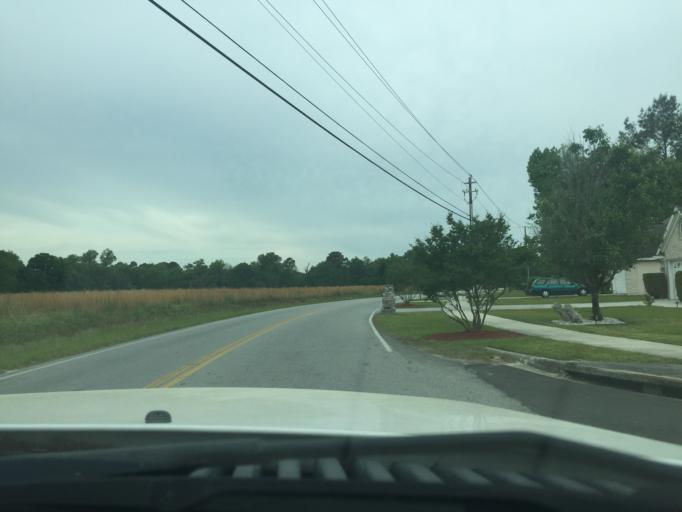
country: US
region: Georgia
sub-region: Chatham County
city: Georgetown
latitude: 31.9694
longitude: -81.2331
